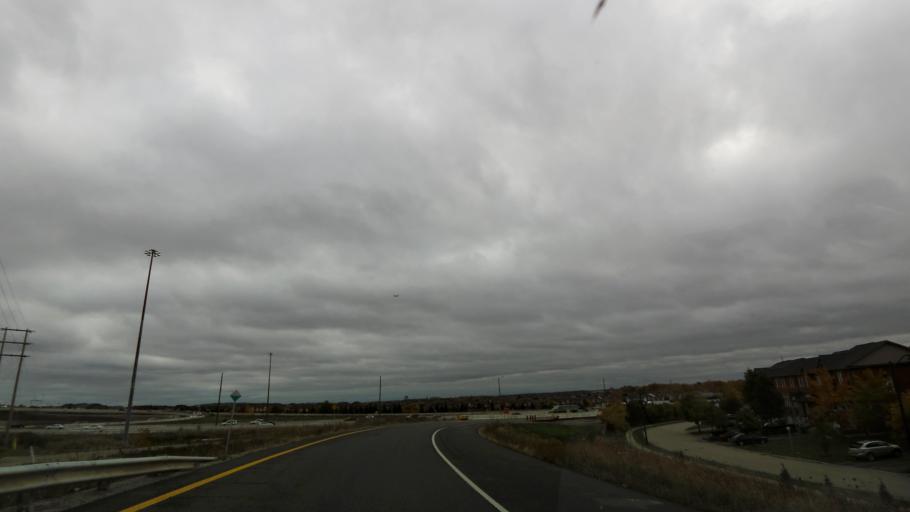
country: CA
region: Ontario
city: Mississauga
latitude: 43.6215
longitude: -79.7098
